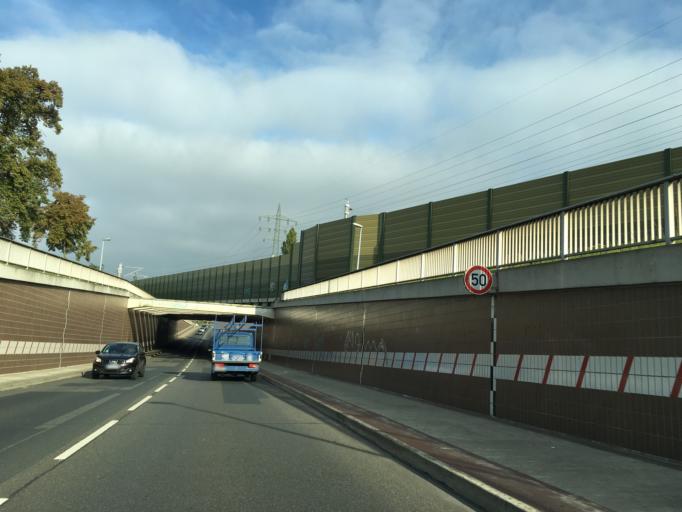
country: DE
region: Lower Saxony
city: Lueneburg
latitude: 53.2720
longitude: 10.4041
